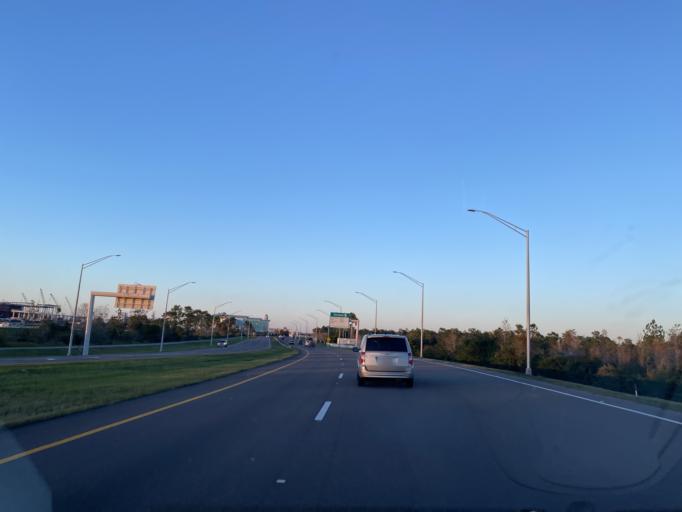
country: US
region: Florida
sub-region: Orange County
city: Meadow Woods
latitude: 28.4020
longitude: -81.3076
